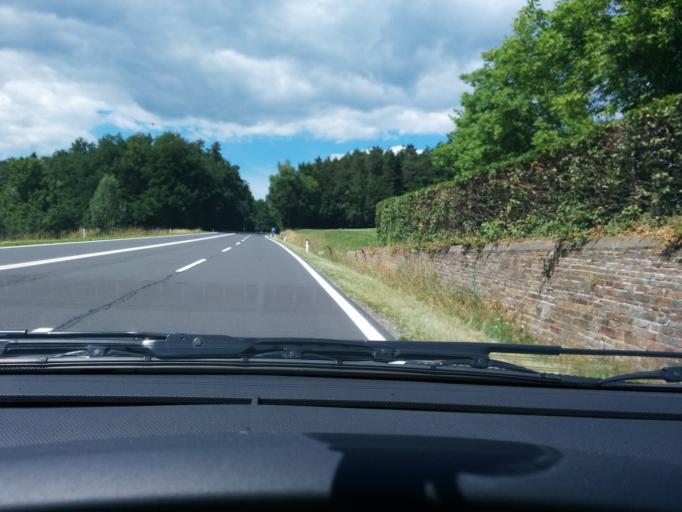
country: AT
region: Styria
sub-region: Politischer Bezirk Hartberg-Fuerstenfeld
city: Grafendorf bei Hartberg
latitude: 47.3478
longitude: 16.0100
